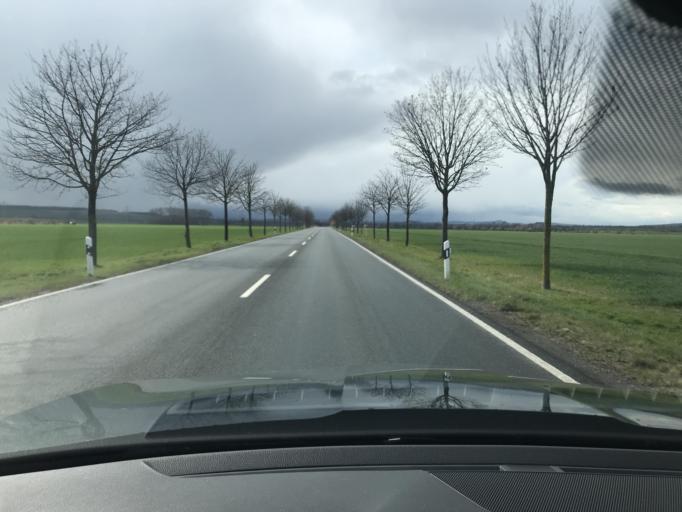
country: DE
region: Saxony-Anhalt
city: Gatersleben
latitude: 51.7861
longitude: 11.2612
